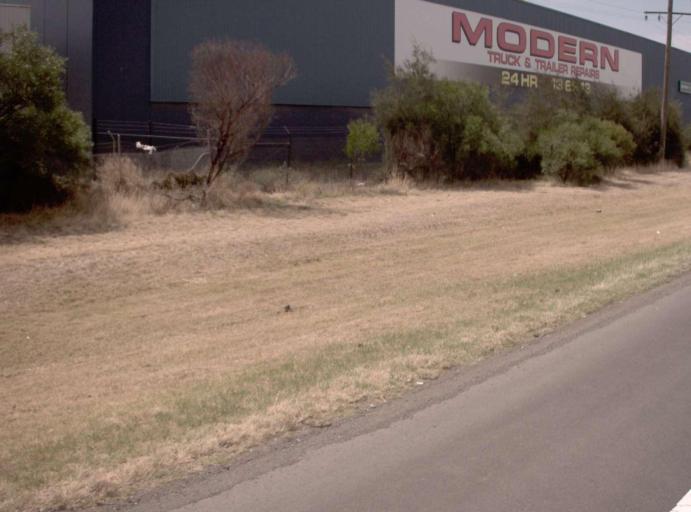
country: AU
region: Victoria
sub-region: Brimbank
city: Brooklyn
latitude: -37.8347
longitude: 144.8057
